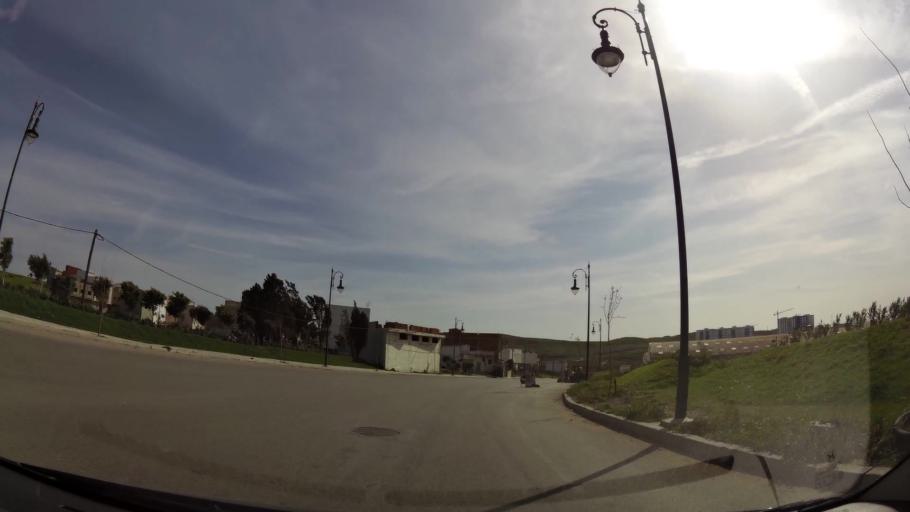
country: MA
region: Tanger-Tetouan
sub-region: Tanger-Assilah
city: Tangier
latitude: 35.7086
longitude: -5.8097
